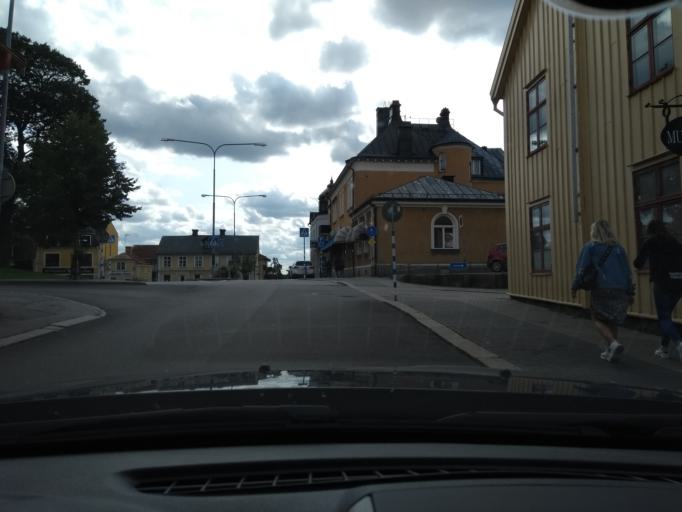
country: SE
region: Kalmar
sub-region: Vimmerby Kommun
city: Vimmerby
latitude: 57.6661
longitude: 15.8565
